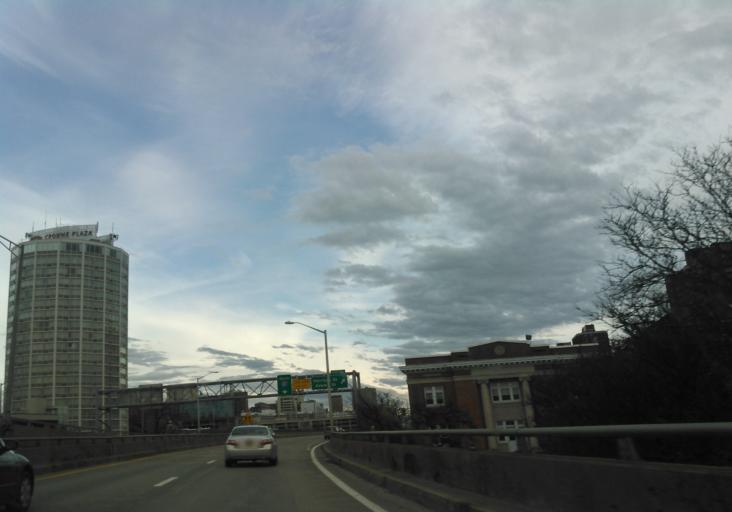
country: US
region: New York
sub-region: Onondaga County
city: Syracuse
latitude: 43.0490
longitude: -76.1431
